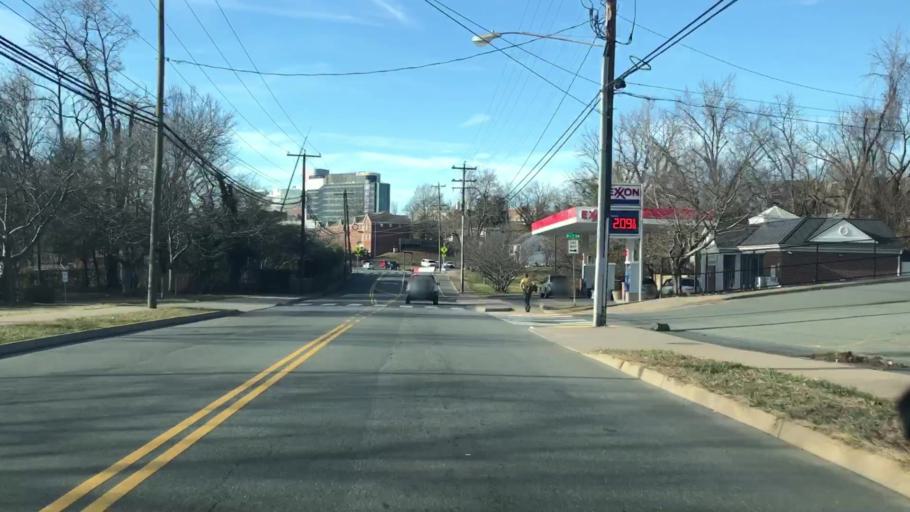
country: US
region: Virginia
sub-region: City of Charlottesville
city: Charlottesville
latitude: 38.0275
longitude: -78.4913
